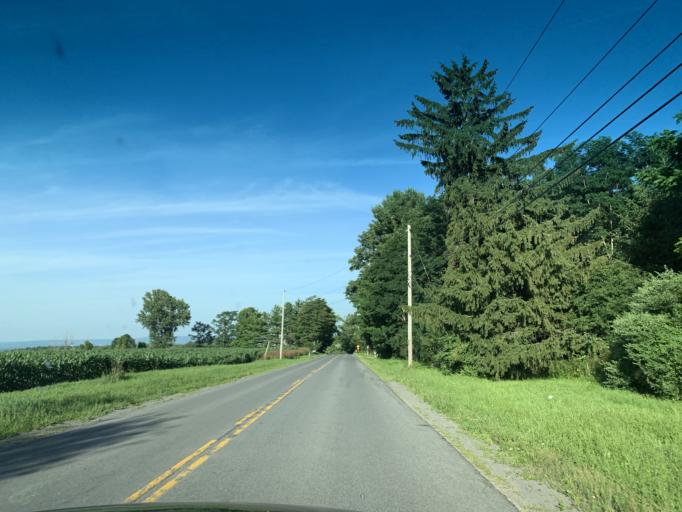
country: US
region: New York
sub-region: Oneida County
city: Clinton
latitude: 43.0550
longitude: -75.4396
